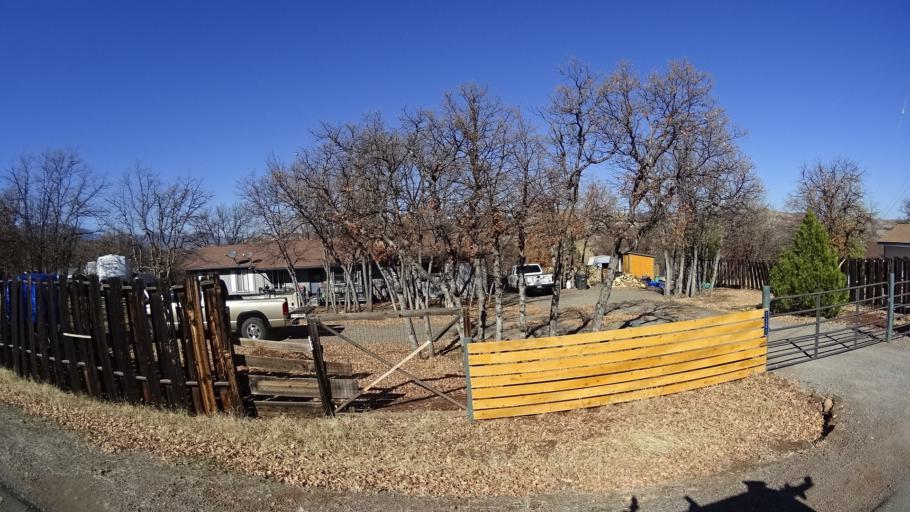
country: US
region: California
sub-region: Siskiyou County
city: Montague
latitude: 41.8869
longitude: -122.4868
